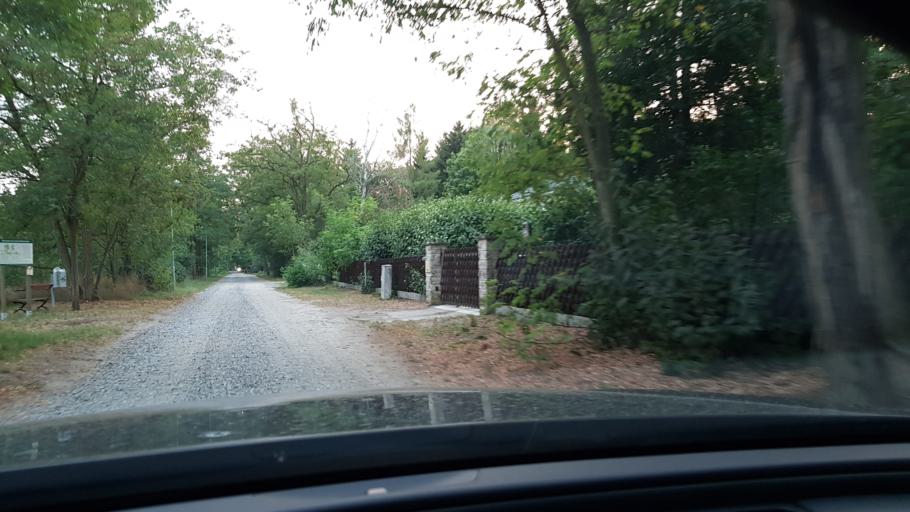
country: DE
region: Berlin
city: Friedrichshagen
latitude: 52.4780
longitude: 13.6274
